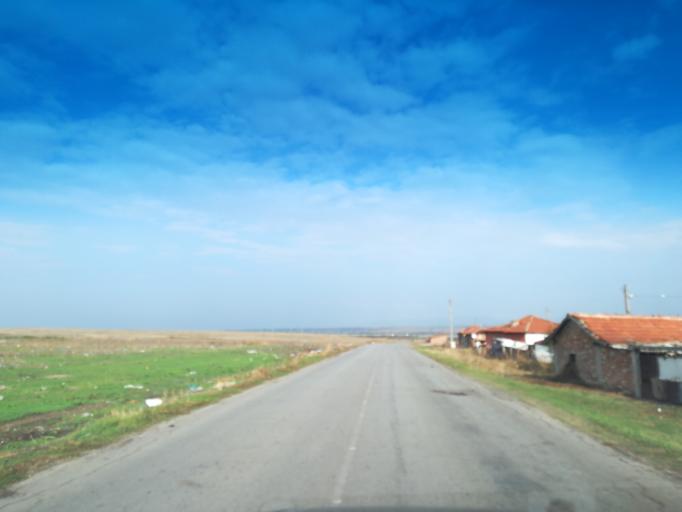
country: BG
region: Stara Zagora
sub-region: Obshtina Chirpan
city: Chirpan
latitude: 42.2011
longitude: 25.3097
